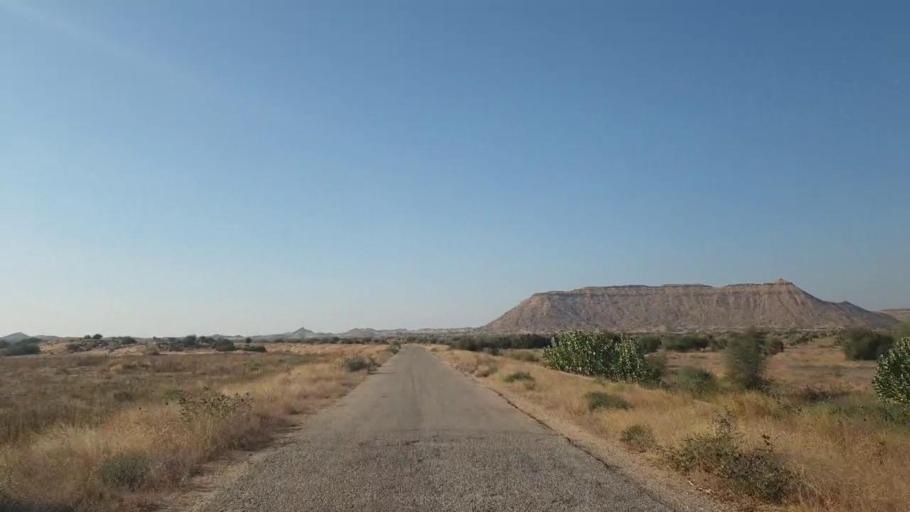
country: PK
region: Sindh
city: Malir Cantonment
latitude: 25.3922
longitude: 67.5136
